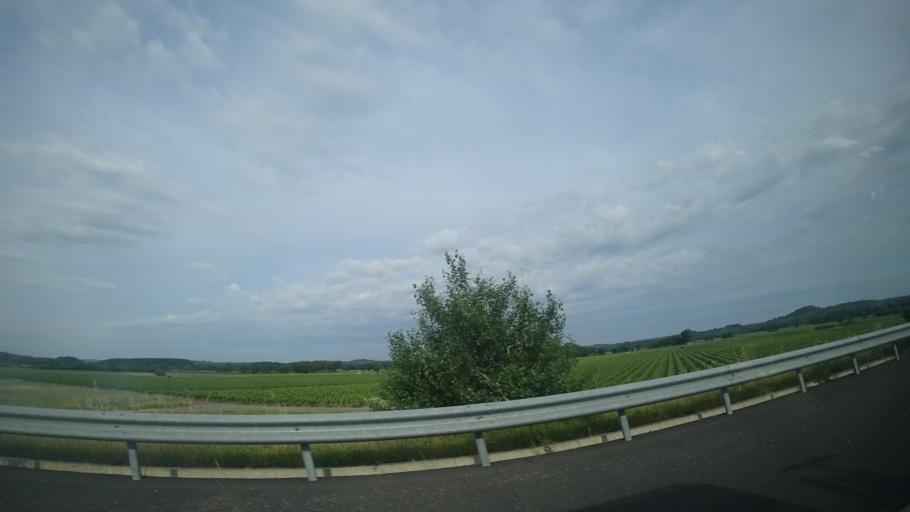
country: FR
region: Languedoc-Roussillon
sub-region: Departement de l'Herault
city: Lezignan-la-Cebe
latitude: 43.4956
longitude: 3.4466
